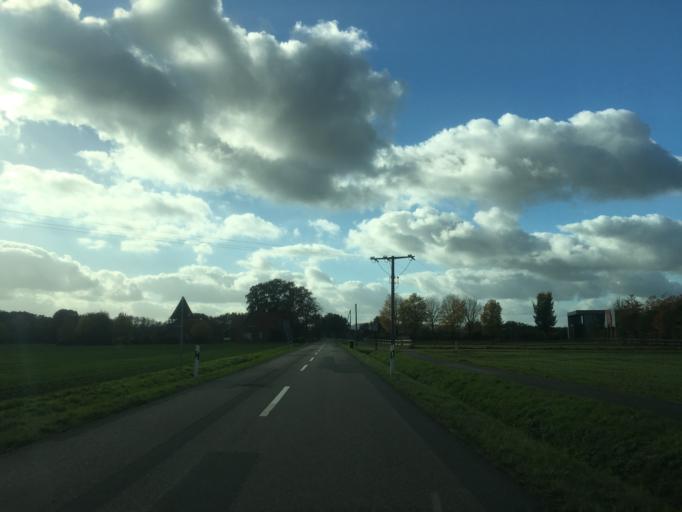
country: DE
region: North Rhine-Westphalia
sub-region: Regierungsbezirk Munster
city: Havixbeck
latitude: 51.9922
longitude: 7.4347
